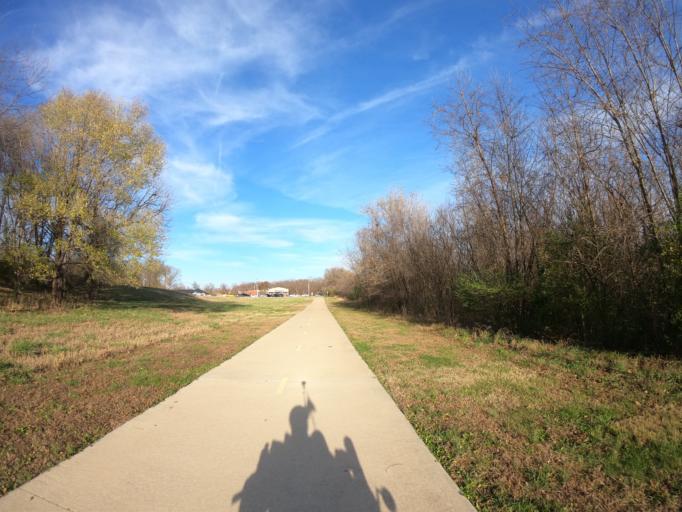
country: US
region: Arkansas
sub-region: Benton County
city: Rogers
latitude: 36.3332
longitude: -94.1640
